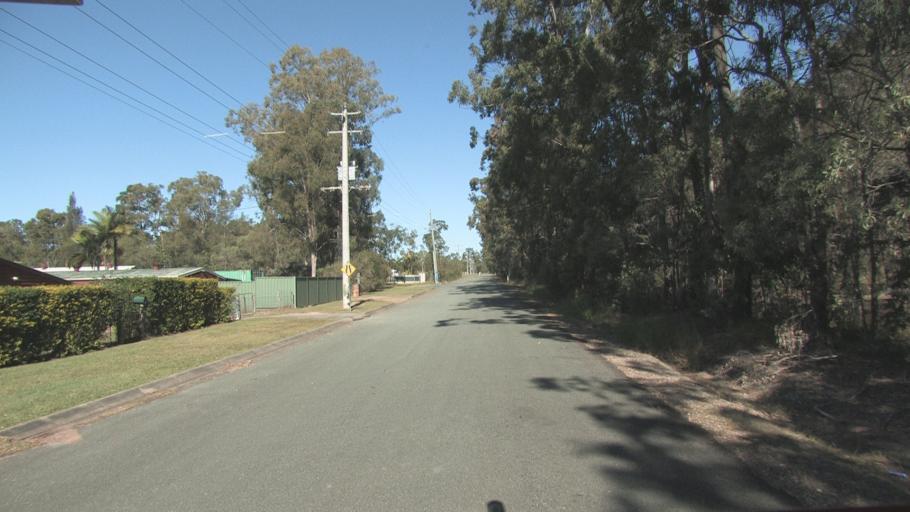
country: AU
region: Queensland
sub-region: Logan
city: Park Ridge South
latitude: -27.6977
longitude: 153.0041
